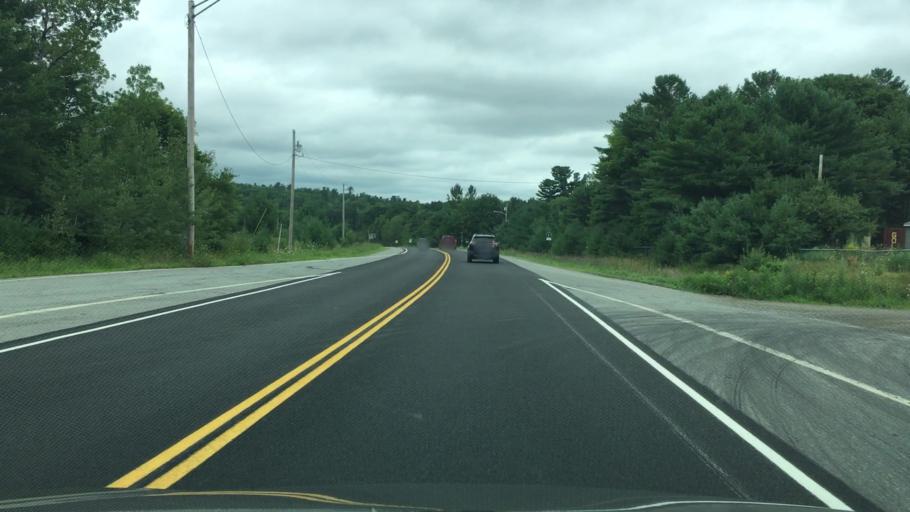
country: US
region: Maine
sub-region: Penobscot County
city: Orrington
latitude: 44.6947
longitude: -68.8139
